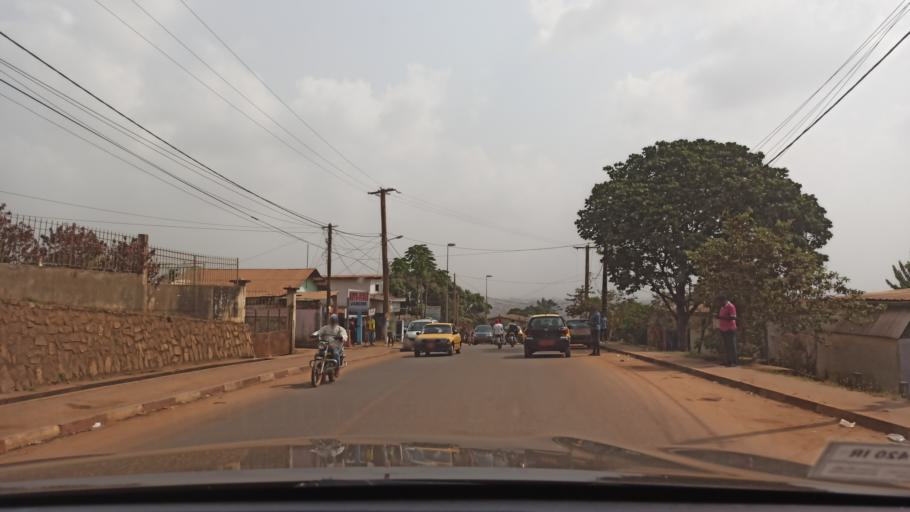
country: CM
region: Centre
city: Yaounde
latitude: 3.8780
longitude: 11.4860
